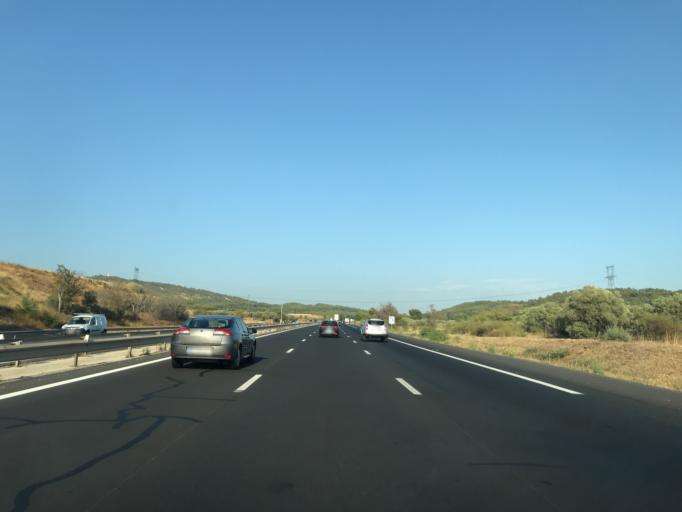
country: FR
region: Provence-Alpes-Cote d'Azur
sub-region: Departement des Bouches-du-Rhone
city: Coudoux
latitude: 43.5536
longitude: 5.2581
